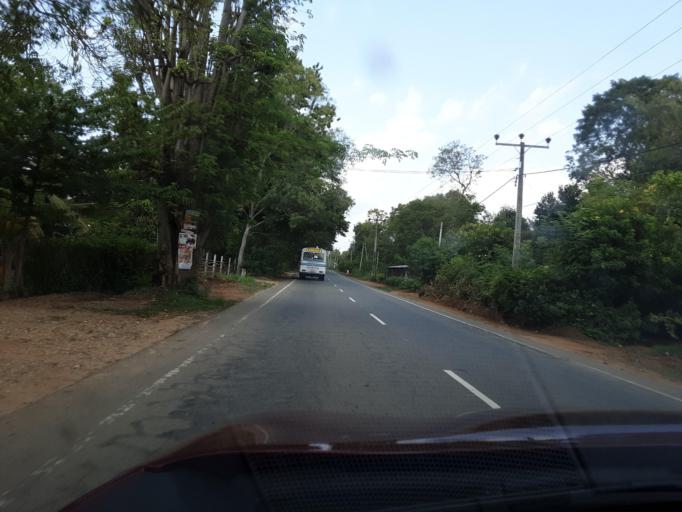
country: LK
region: Uva
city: Haputale
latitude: 6.5314
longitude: 81.1298
